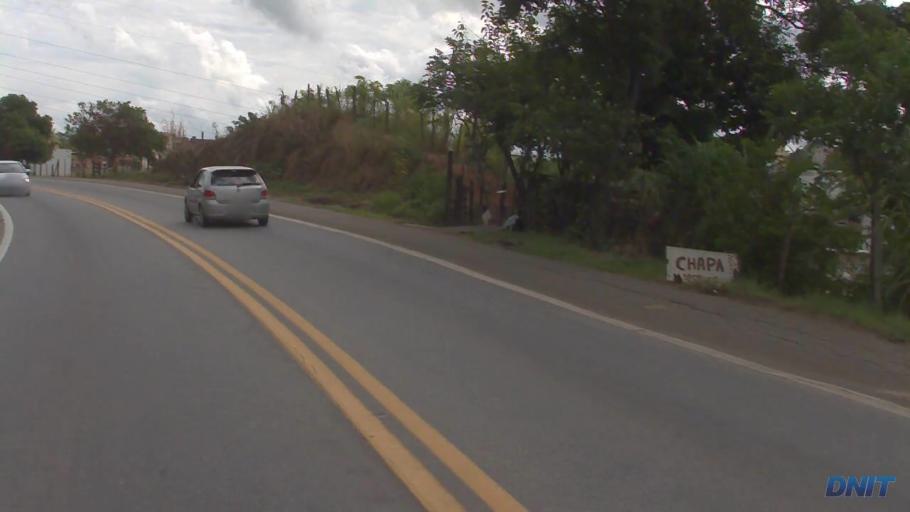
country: BR
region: Minas Gerais
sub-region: Ipatinga
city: Ipatinga
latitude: -19.4578
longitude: -42.5251
